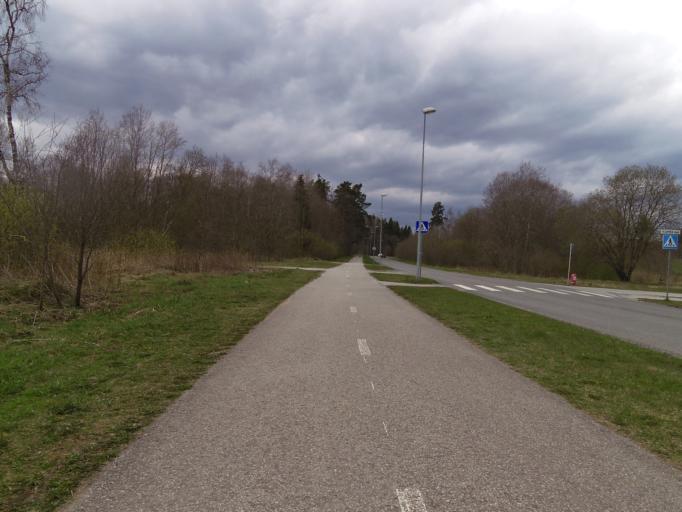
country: EE
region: Harju
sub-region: Kiili vald
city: Kiili
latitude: 59.3581
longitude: 24.8117
